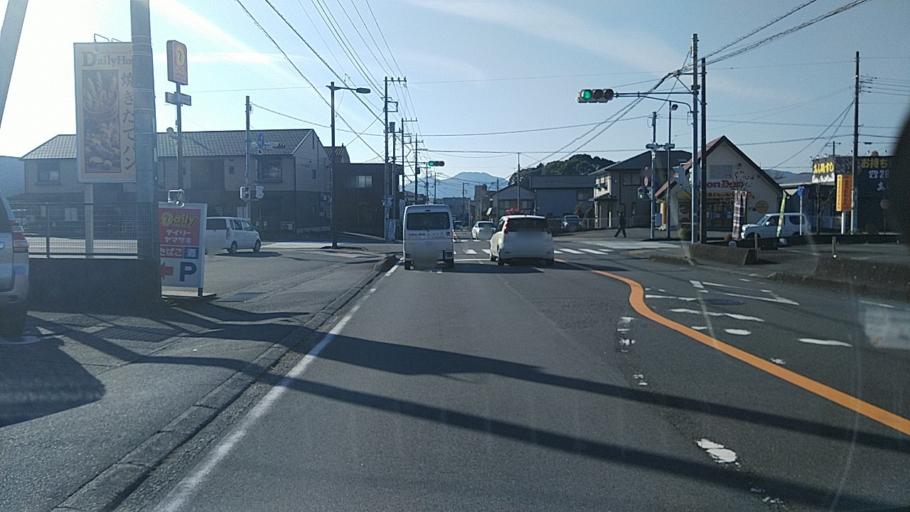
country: JP
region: Shizuoka
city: Fujinomiya
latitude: 35.2323
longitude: 138.6168
